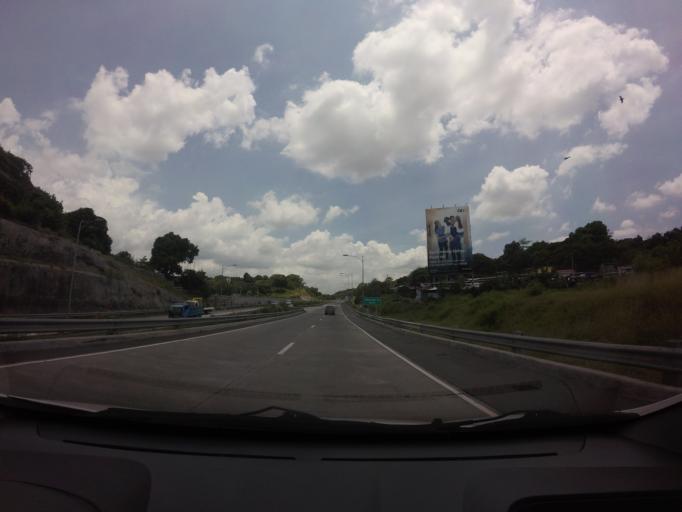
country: PH
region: Calabarzon
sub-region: Province of Laguna
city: San Pedro
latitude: 14.3838
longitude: 121.0381
